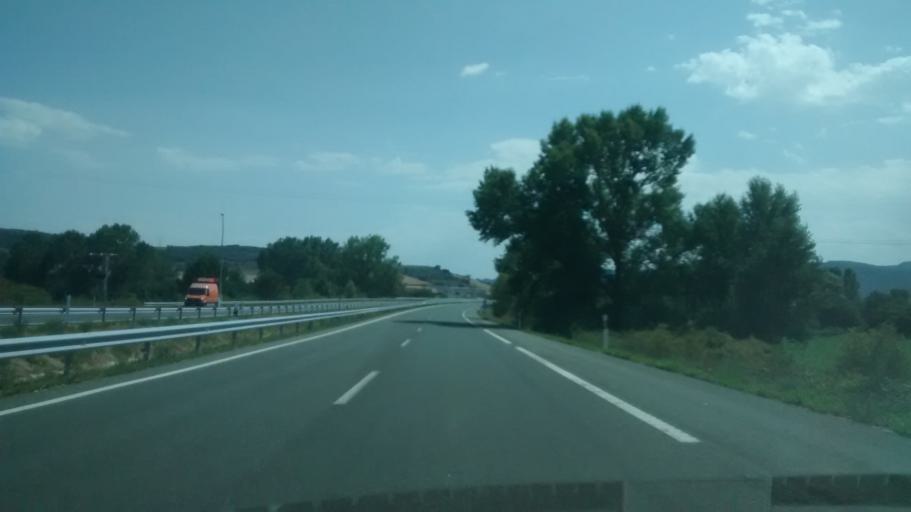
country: ES
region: Basque Country
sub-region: Provincia de Alava
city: Zambrana
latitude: 42.6843
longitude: -2.8908
